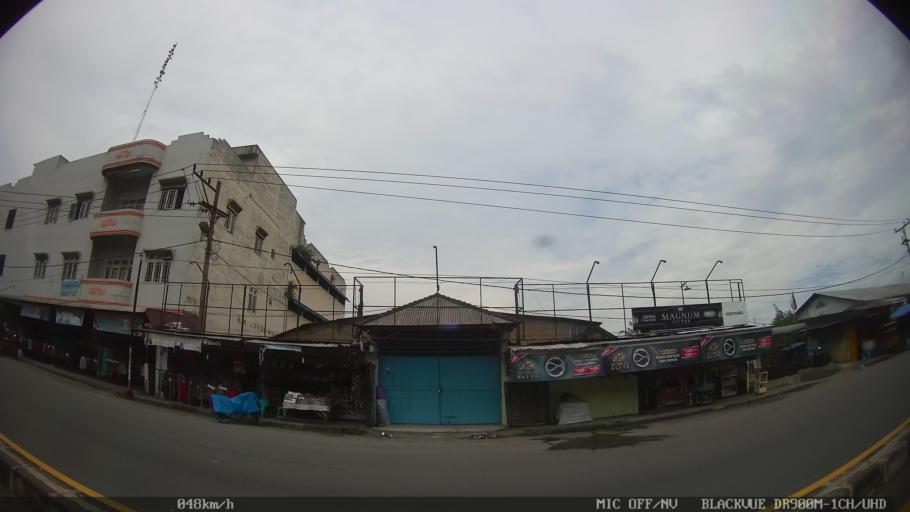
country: ID
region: North Sumatra
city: Sunggal
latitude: 3.6005
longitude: 98.5751
